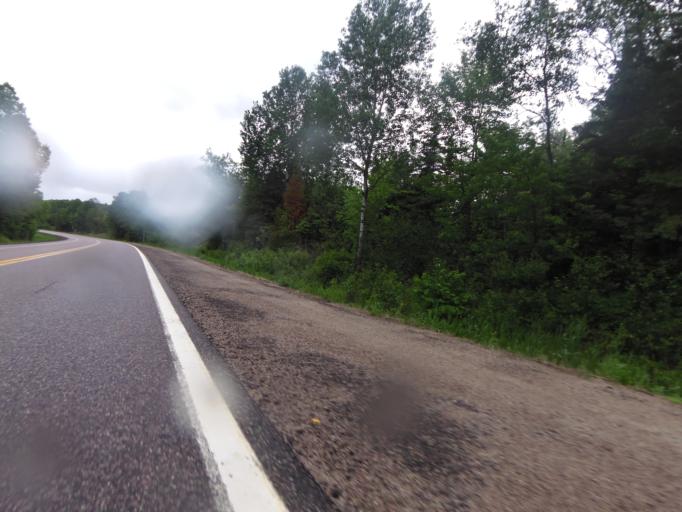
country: CA
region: Quebec
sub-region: Outaouais
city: Shawville
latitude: 45.9261
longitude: -76.2447
